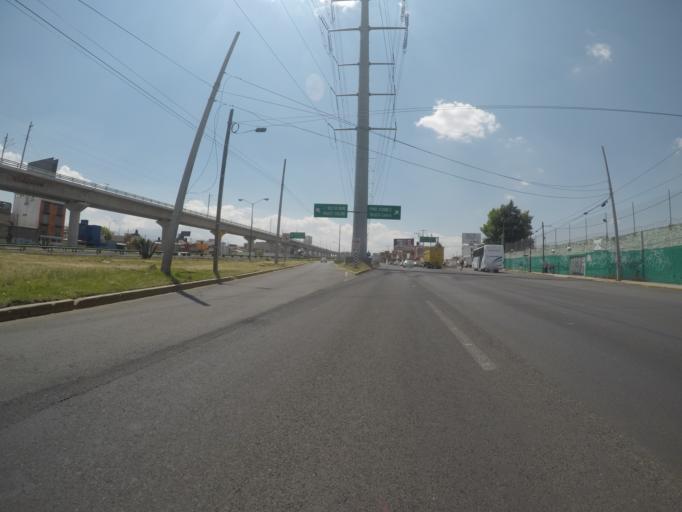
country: MX
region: Mexico
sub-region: Metepec
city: San Jorge Pueblo Nuevo
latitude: 19.2726
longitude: -99.6336
